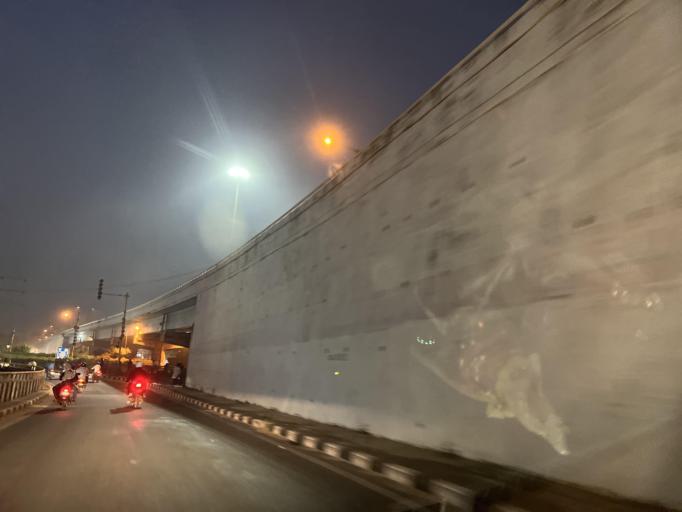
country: IN
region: Odisha
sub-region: Cuttack
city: Cuttack
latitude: 20.4558
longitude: 85.9012
